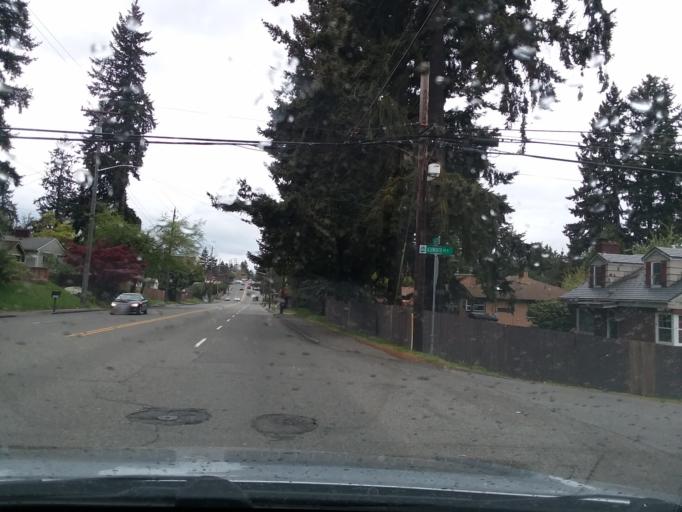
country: US
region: Washington
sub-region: King County
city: Shoreline
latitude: 47.7342
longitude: -122.3396
